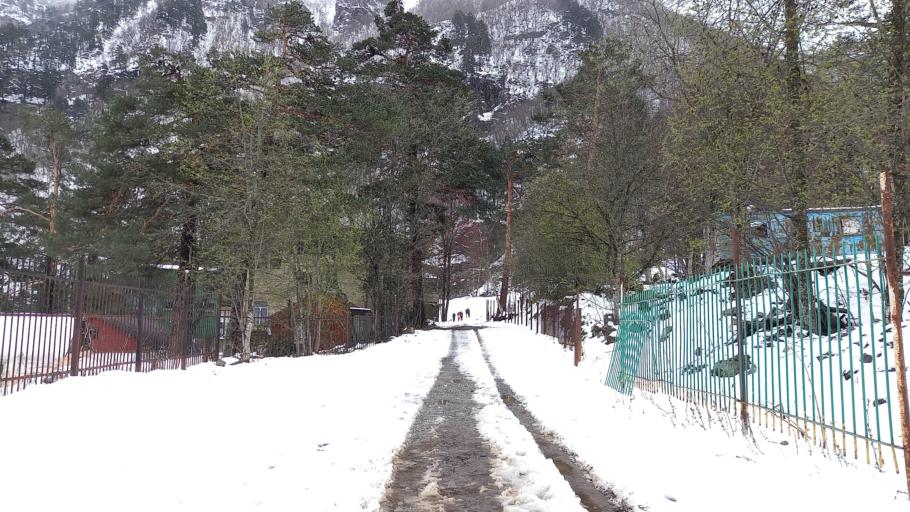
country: RU
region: North Ossetia
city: Mizur
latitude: 42.7855
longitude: 43.9042
